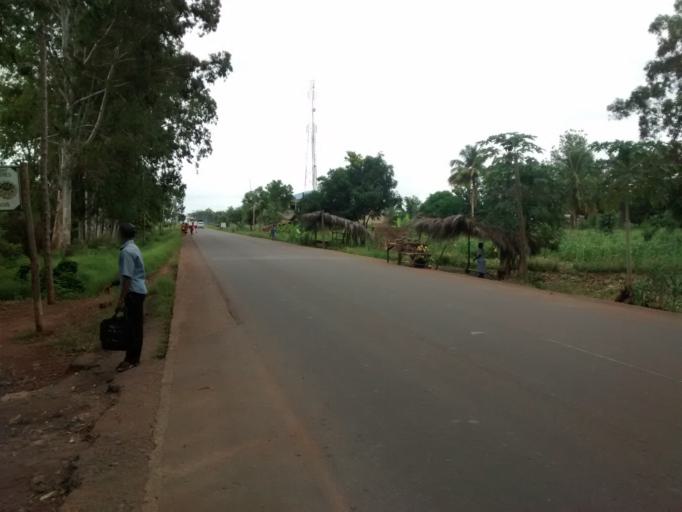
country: TG
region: Maritime
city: Tsevie
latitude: 6.3805
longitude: 1.2040
